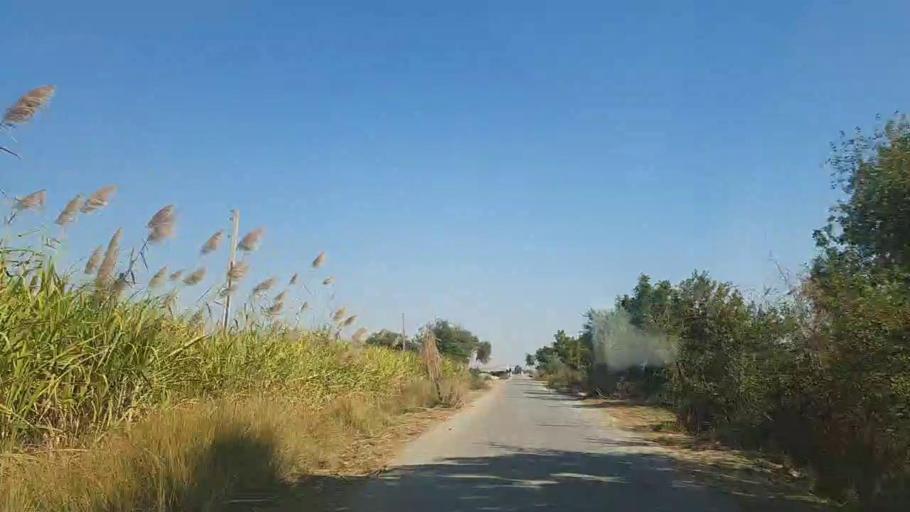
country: PK
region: Sindh
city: Sanghar
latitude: 26.2207
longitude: 68.9474
